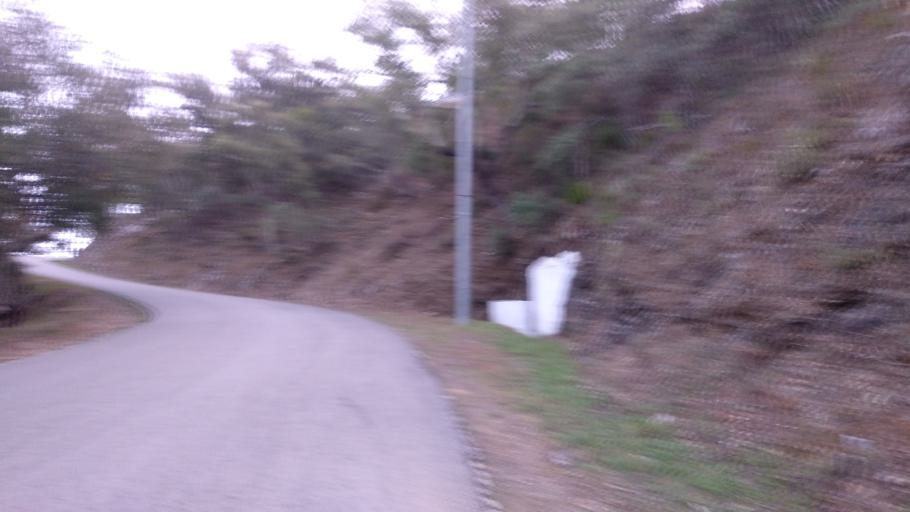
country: PT
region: Faro
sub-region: Sao Bras de Alportel
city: Sao Bras de Alportel
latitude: 37.1806
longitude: -7.9122
